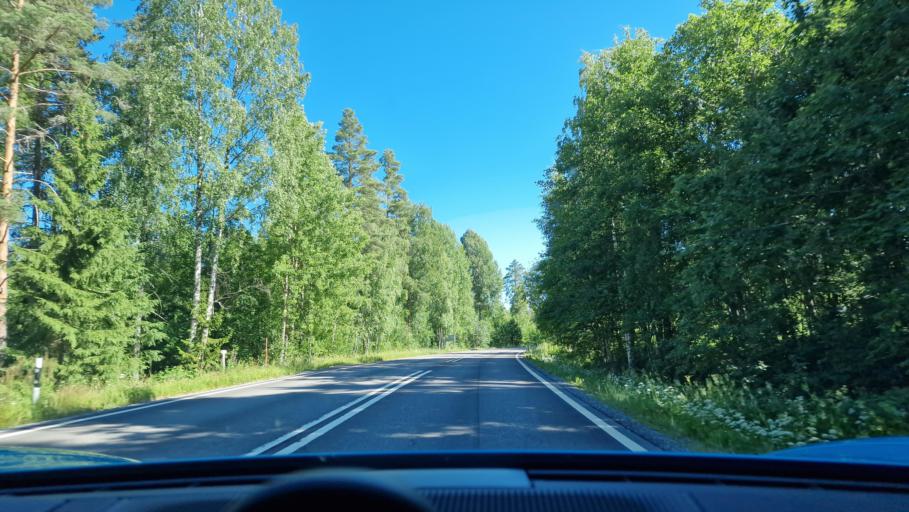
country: FI
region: Pirkanmaa
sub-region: Tampere
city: Sahalahti
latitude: 61.5196
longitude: 24.2254
